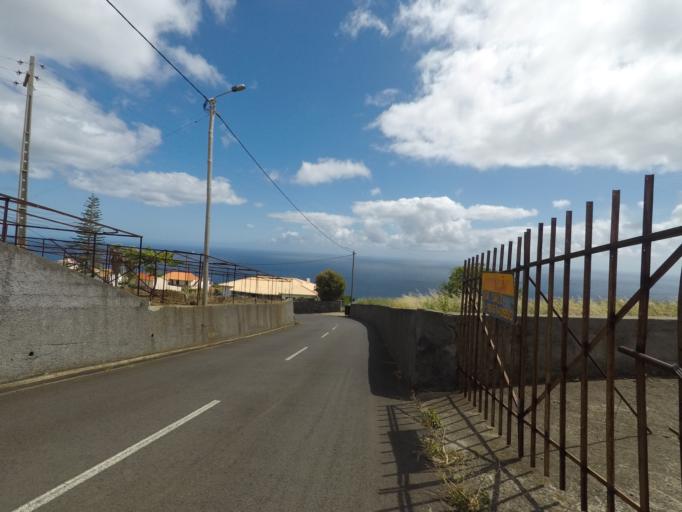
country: PT
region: Madeira
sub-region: Calheta
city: Estreito da Calheta
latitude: 32.7330
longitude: -17.1839
